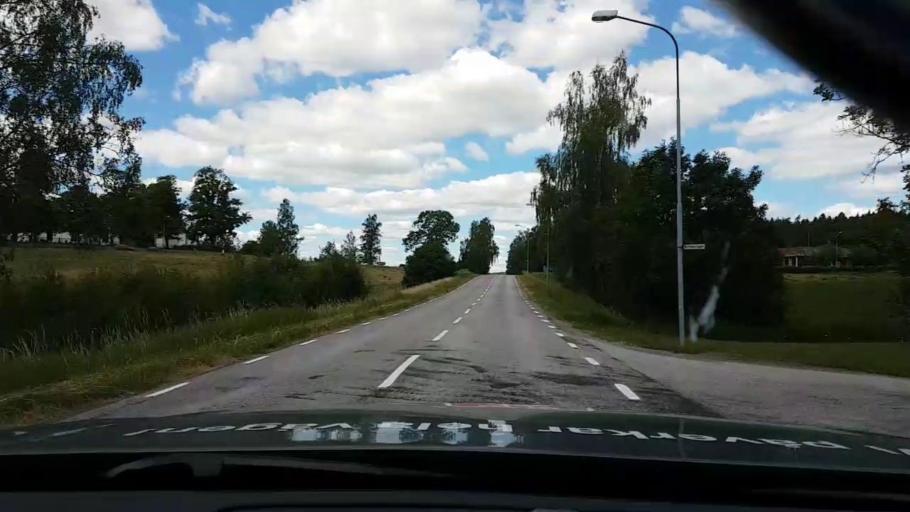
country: SE
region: Kalmar
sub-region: Vasterviks Kommun
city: Overum
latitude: 58.0788
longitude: 16.3557
